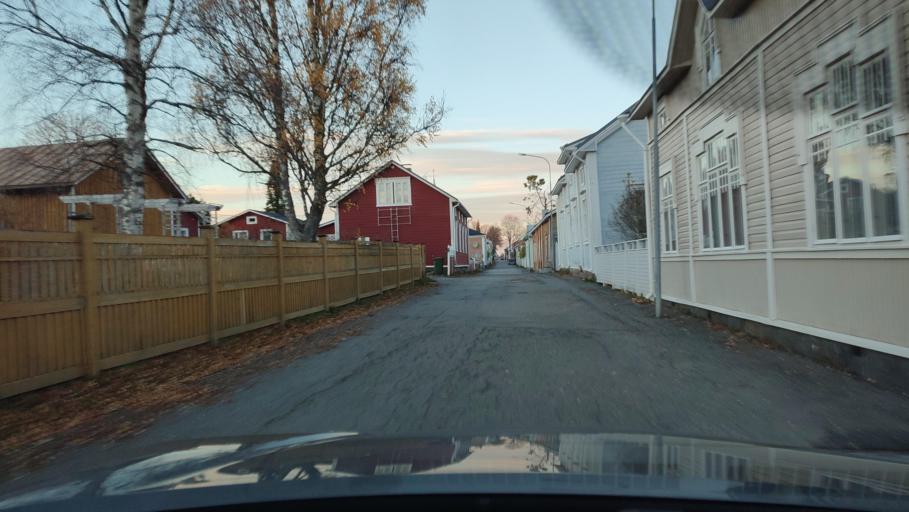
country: FI
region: Ostrobothnia
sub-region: Sydosterbotten
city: Kristinestad
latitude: 62.2696
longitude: 21.3760
